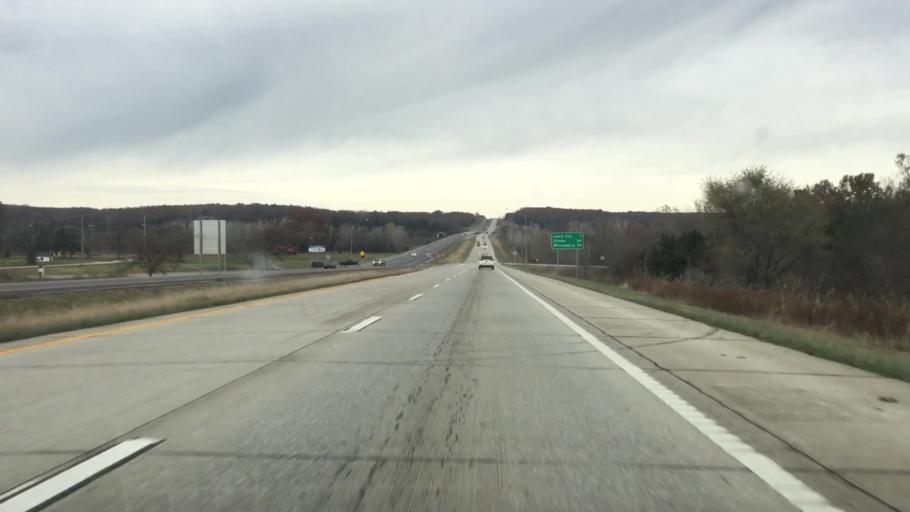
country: US
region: Missouri
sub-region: Saint Clair County
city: Osceola
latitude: 38.0518
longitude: -93.6878
